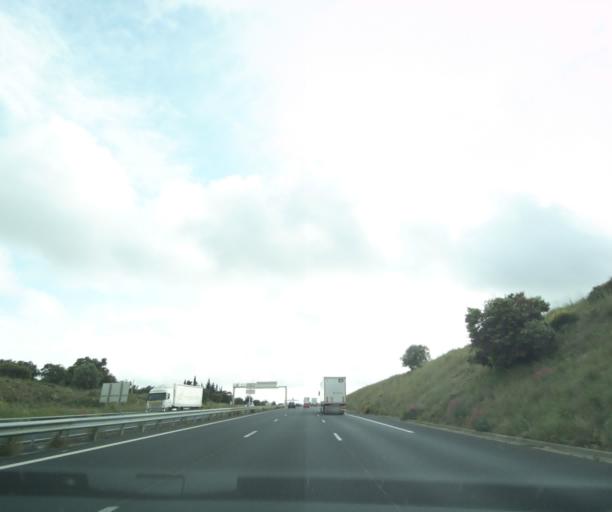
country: FR
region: Languedoc-Roussillon
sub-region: Departement de l'Herault
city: Poussan
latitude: 43.4760
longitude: 3.6519
